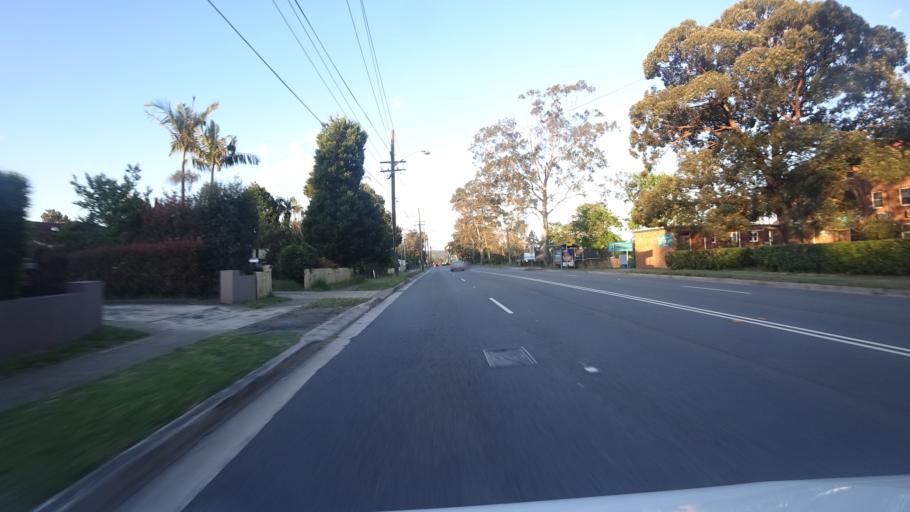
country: AU
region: New South Wales
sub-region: Ryde
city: North Ryde
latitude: -33.7982
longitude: 151.1228
